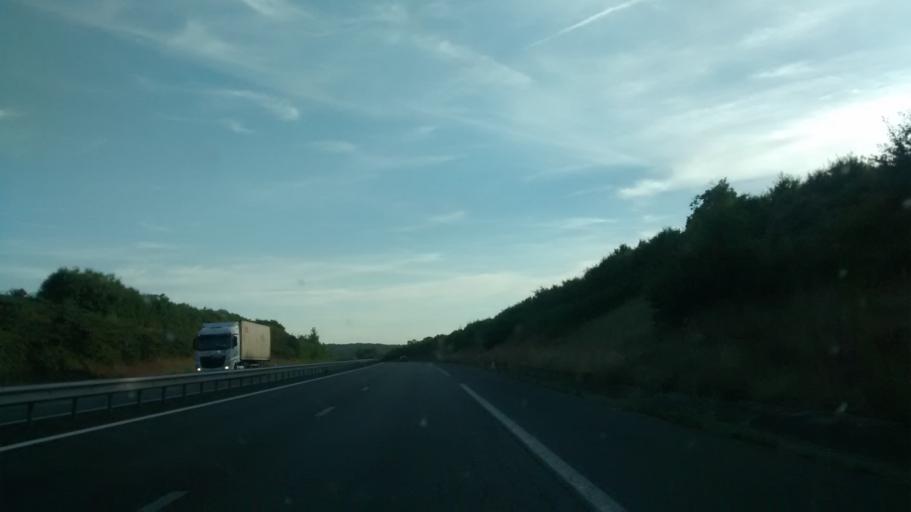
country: FR
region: Brittany
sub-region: Departement d'Ille-et-Vilaine
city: Saint-Jean-sur-Couesnon
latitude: 48.2850
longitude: -1.3880
